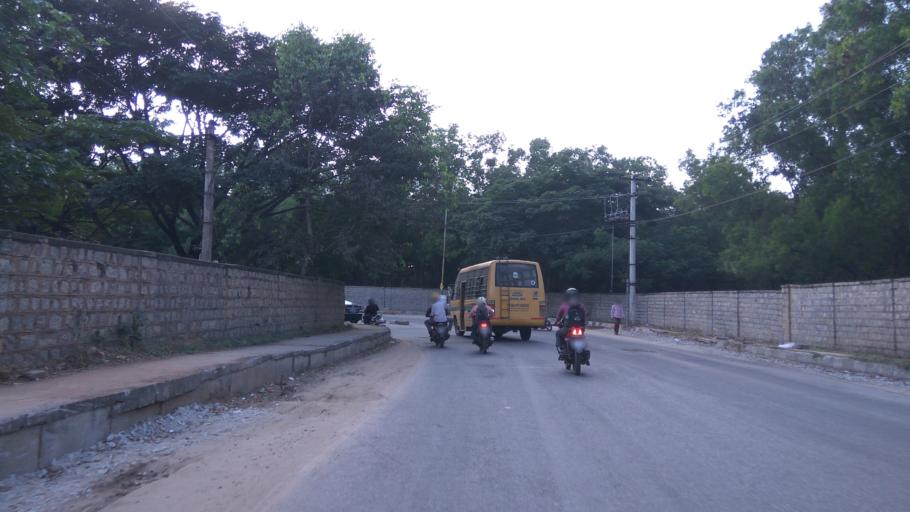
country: IN
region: Karnataka
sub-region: Bangalore Urban
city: Bangalore
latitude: 12.9637
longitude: 77.6907
